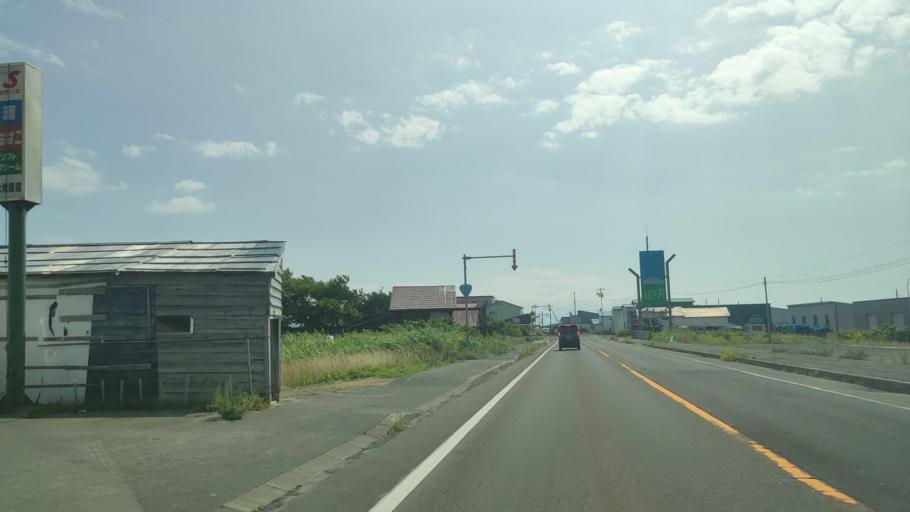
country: JP
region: Hokkaido
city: Rumoi
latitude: 43.9984
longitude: 141.6542
